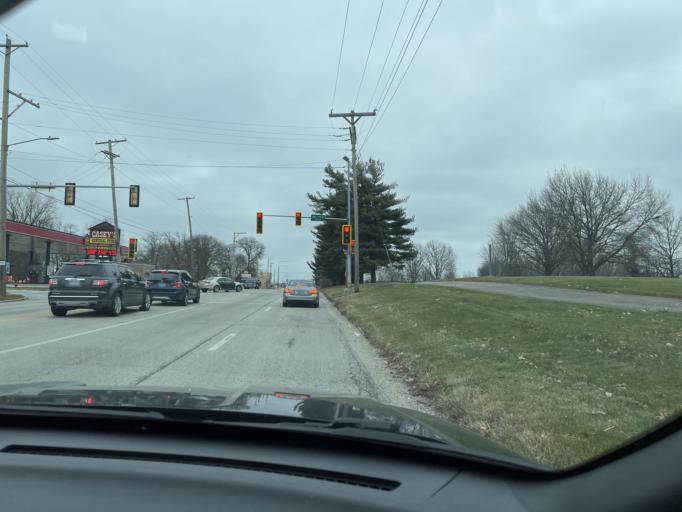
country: US
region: Illinois
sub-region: Sangamon County
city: Grandview
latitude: 39.8019
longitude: -89.6113
